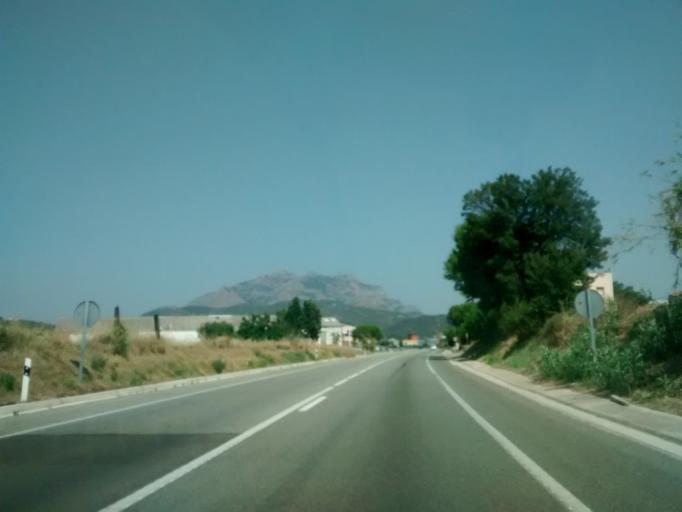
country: ES
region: Catalonia
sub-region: Provincia de Barcelona
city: Olesa de Montserrat
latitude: 41.5399
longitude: 1.8883
